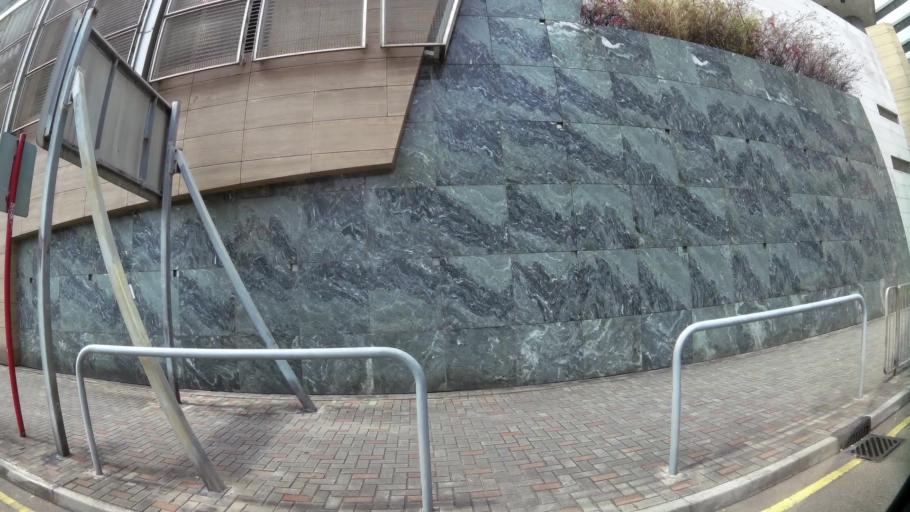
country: HK
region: Wanchai
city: Wan Chai
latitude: 22.2839
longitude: 114.2249
